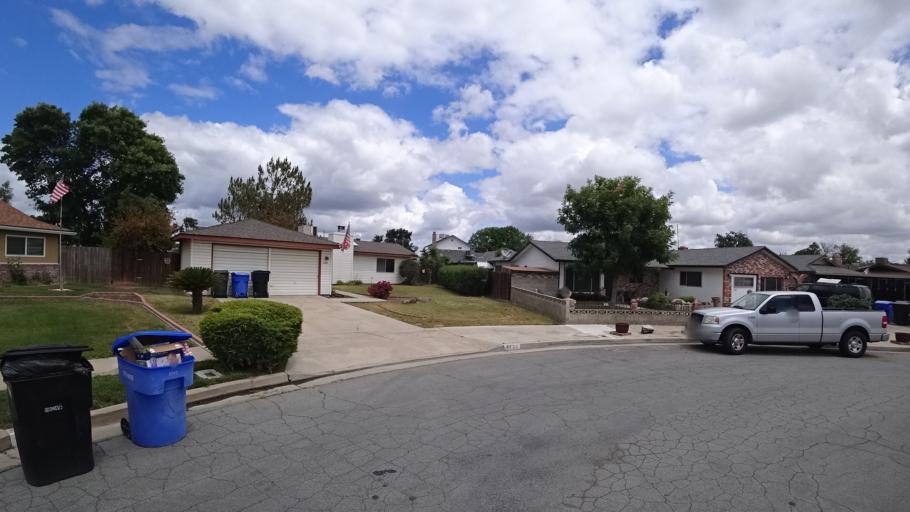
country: US
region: California
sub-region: Kings County
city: Hanford
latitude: 36.3405
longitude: -119.6276
